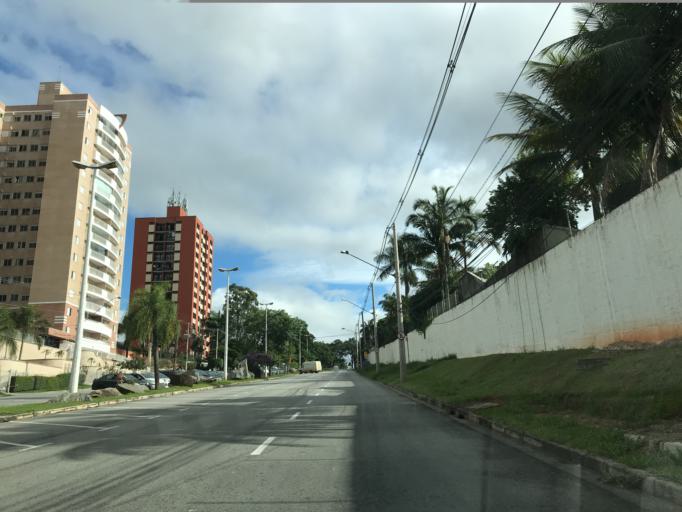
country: BR
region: Sao Paulo
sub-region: Carapicuiba
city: Carapicuiba
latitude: -23.4900
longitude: -46.8346
